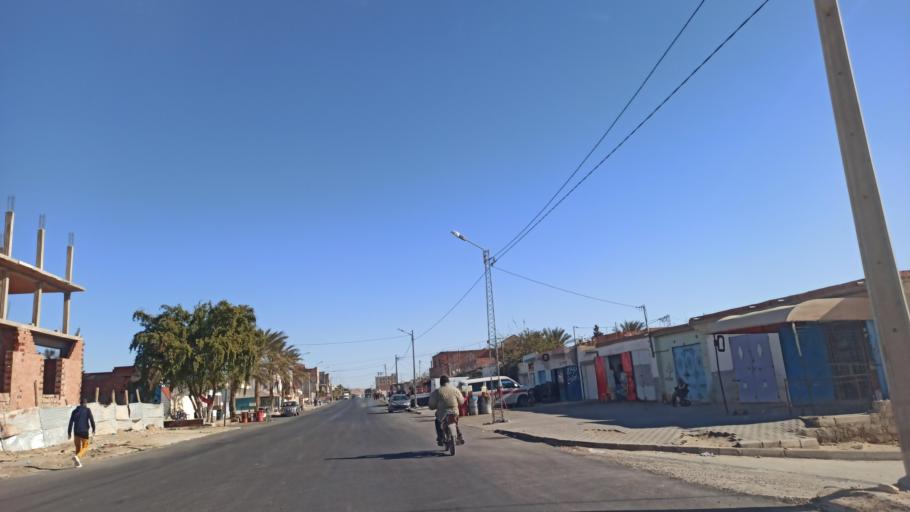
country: TN
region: Gafsa
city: Al Metlaoui
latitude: 34.3116
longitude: 8.3836
